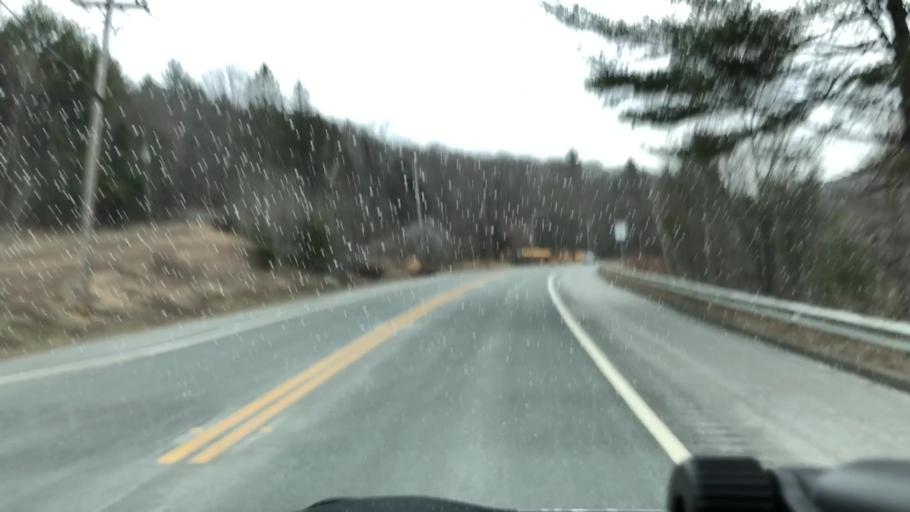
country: US
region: Massachusetts
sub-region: Hampshire County
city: Chesterfield
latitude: 42.4901
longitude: -72.9523
